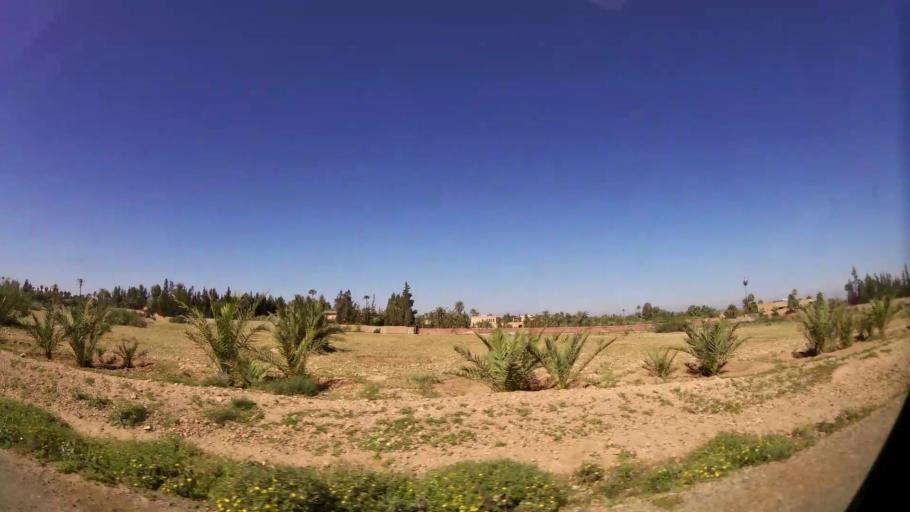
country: MA
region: Marrakech-Tensift-Al Haouz
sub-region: Marrakech
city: Marrakesh
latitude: 31.6698
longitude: -7.9564
